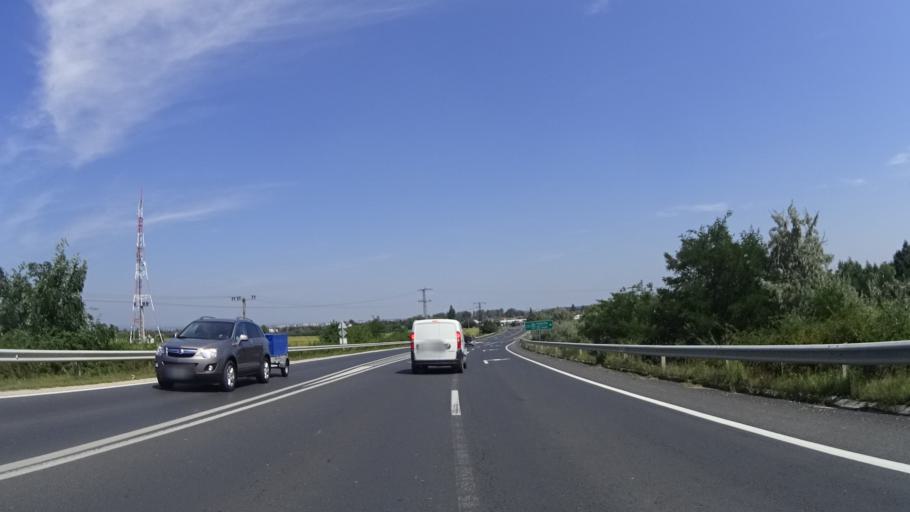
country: HU
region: Fejer
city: Szabadbattyan
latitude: 47.1496
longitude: 18.3960
